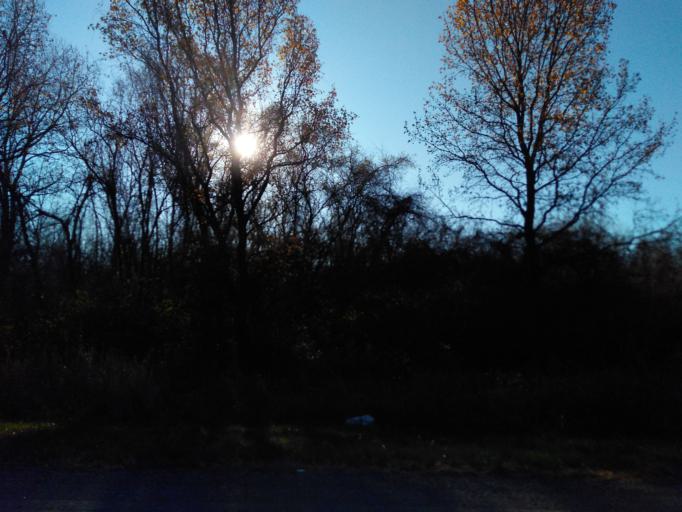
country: US
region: Illinois
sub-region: Saint Clair County
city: Alorton
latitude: 38.5886
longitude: -90.0969
